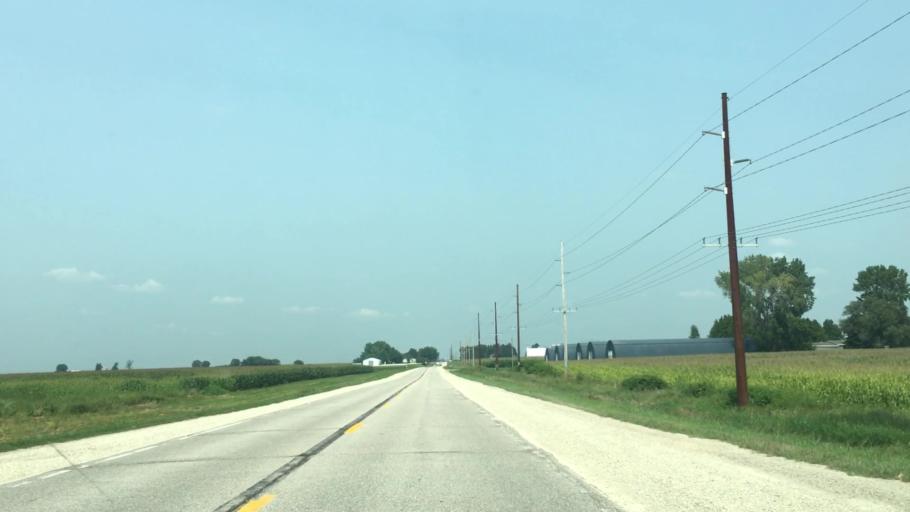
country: US
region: Iowa
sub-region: Buchanan County
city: Independence
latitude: 42.4115
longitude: -91.8899
